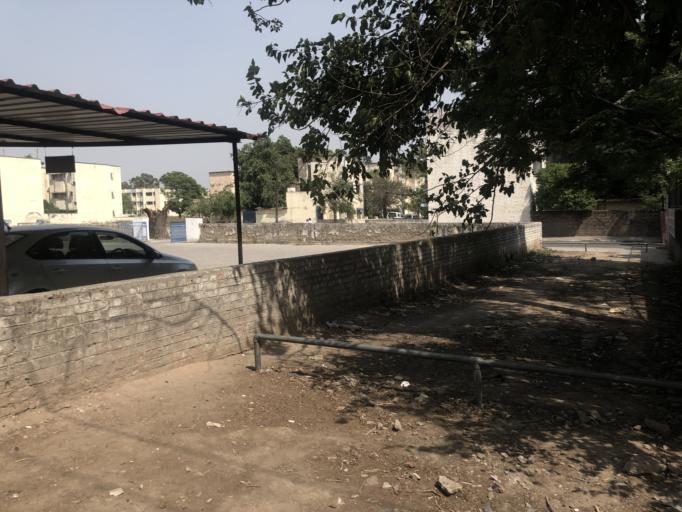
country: IN
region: Chandigarh
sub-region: Chandigarh
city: Chandigarh
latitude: 30.7003
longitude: 76.7699
